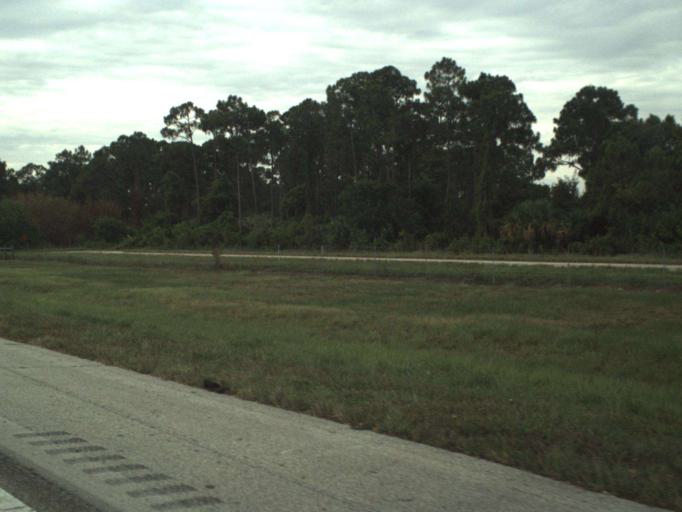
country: US
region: Florida
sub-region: Martin County
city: Palm City
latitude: 27.1430
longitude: -80.3728
